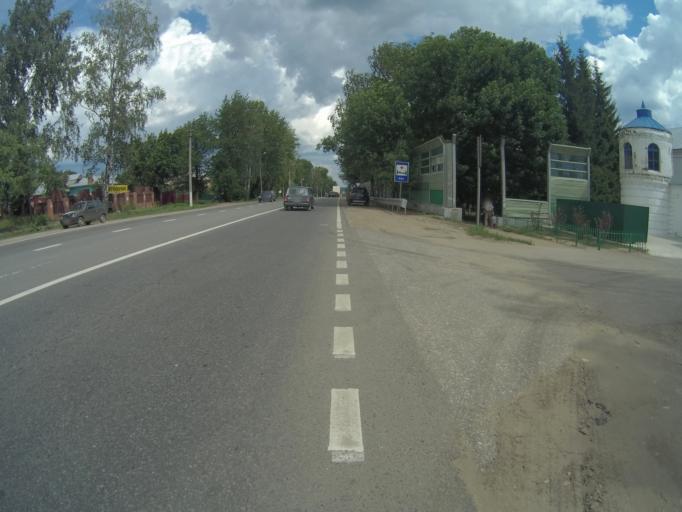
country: RU
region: Vladimir
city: Bogolyubovo
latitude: 56.1973
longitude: 40.5379
